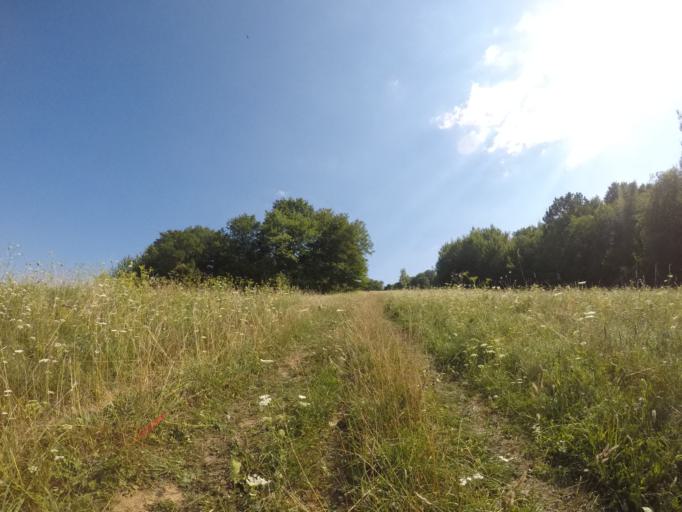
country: SK
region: Presovsky
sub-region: Okres Presov
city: Presov
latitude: 48.9406
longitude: 21.1670
